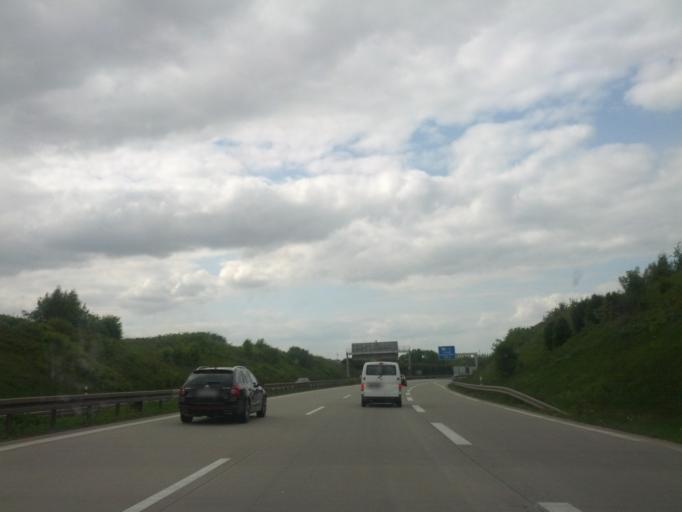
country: DE
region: Saxony
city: Freital
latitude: 51.0400
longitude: 13.6095
